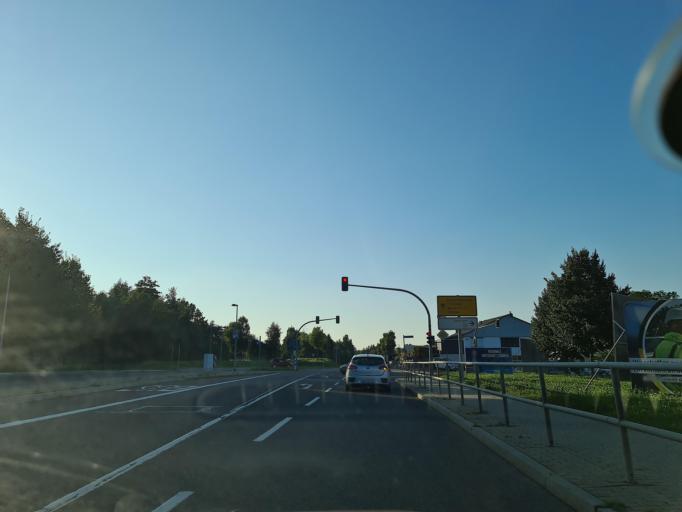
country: DE
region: Saxony
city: Olbernhau
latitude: 50.6568
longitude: 13.3366
